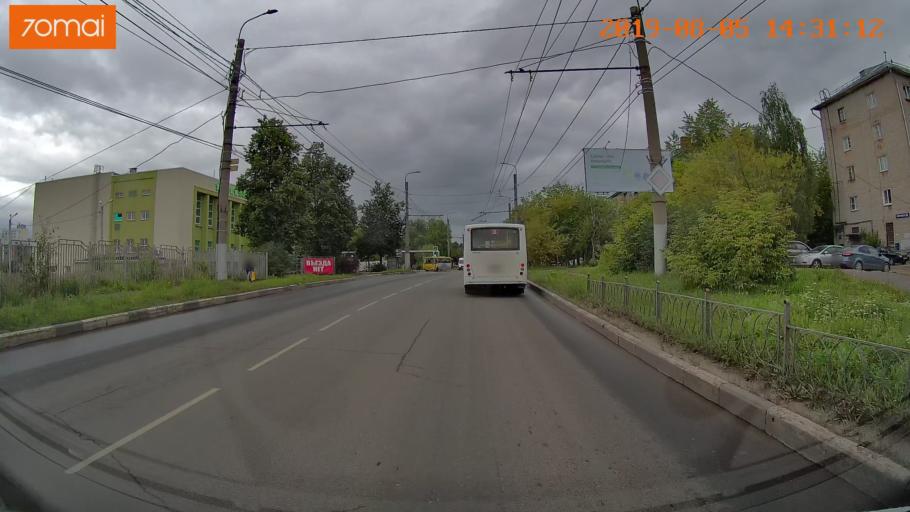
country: RU
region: Ivanovo
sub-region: Gorod Ivanovo
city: Ivanovo
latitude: 56.9860
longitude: 41.0045
